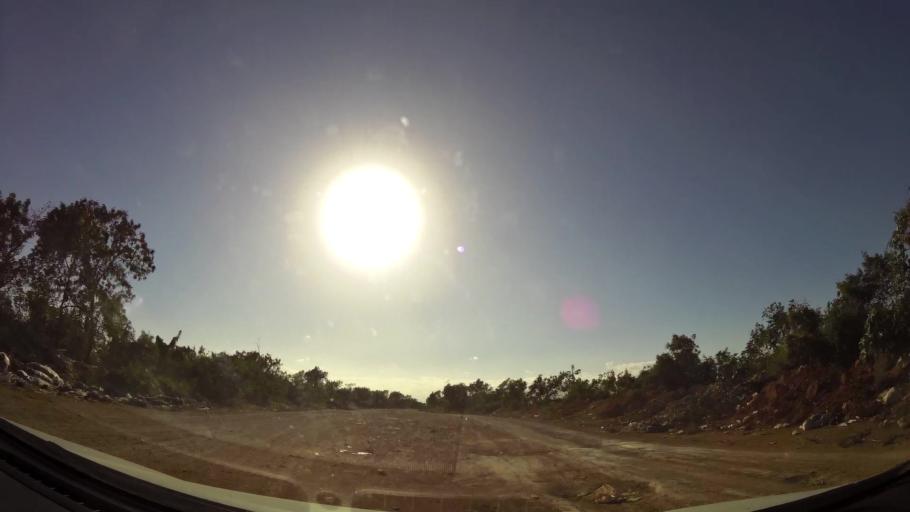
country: DO
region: Santo Domingo
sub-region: Santo Domingo
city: Santo Domingo Este
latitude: 18.4831
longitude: -69.8011
